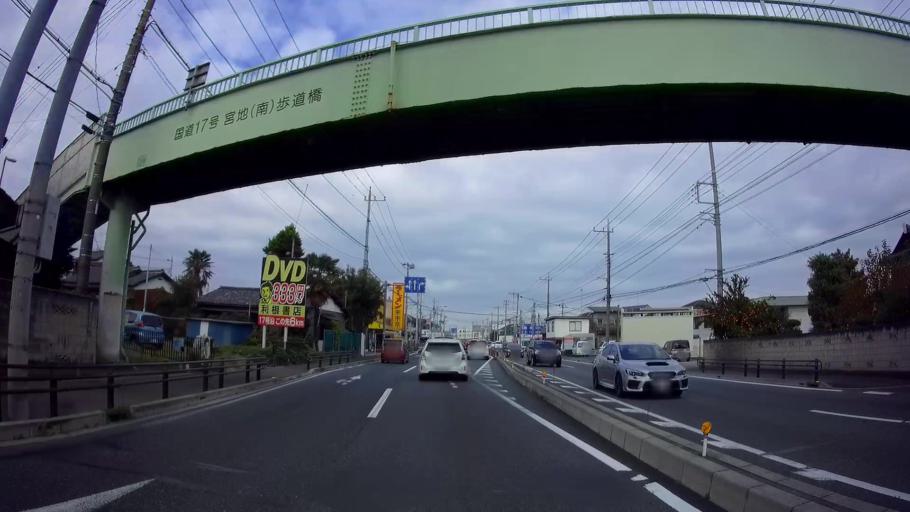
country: JP
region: Saitama
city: Konosu
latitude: 36.0662
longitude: 139.5125
